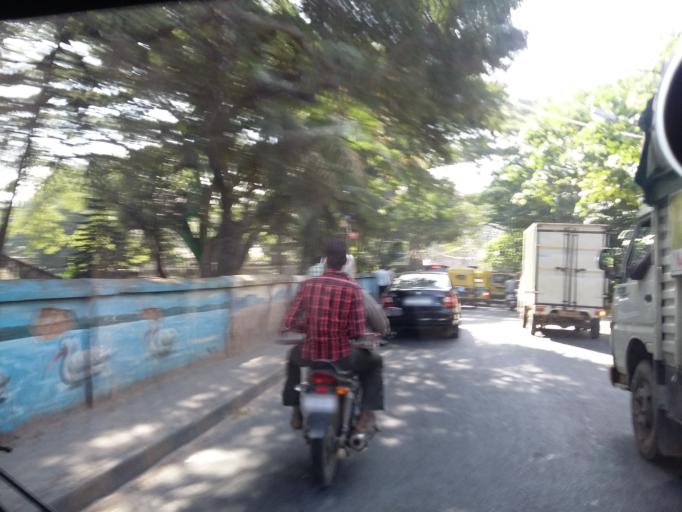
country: IN
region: Karnataka
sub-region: Bangalore Urban
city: Bangalore
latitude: 12.9917
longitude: 77.5990
